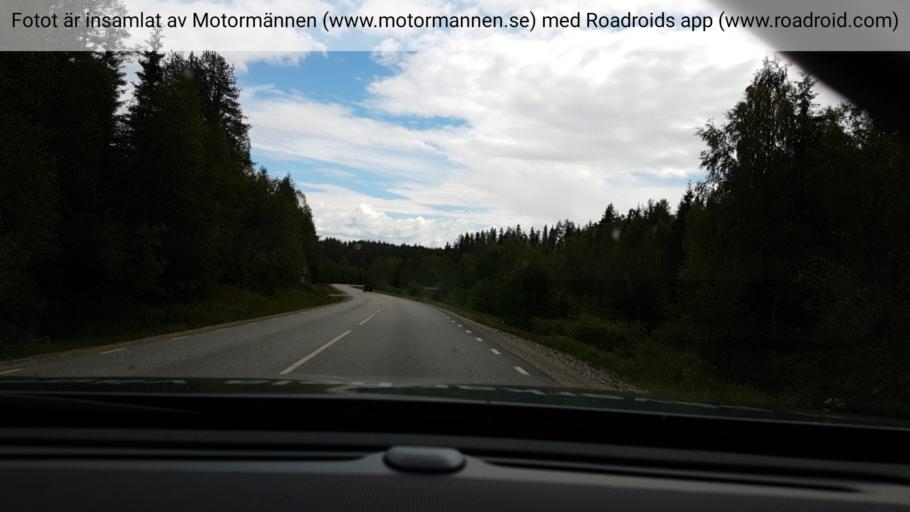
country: SE
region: Vaesterbotten
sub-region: Vindelns Kommun
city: Vindeln
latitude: 64.2070
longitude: 19.6774
